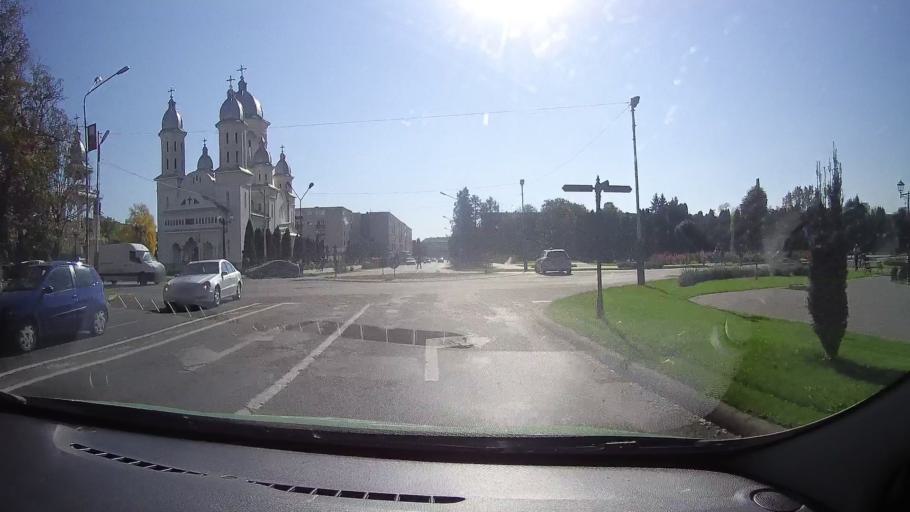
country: RO
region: Satu Mare
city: Carei
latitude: 47.6832
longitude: 22.4693
